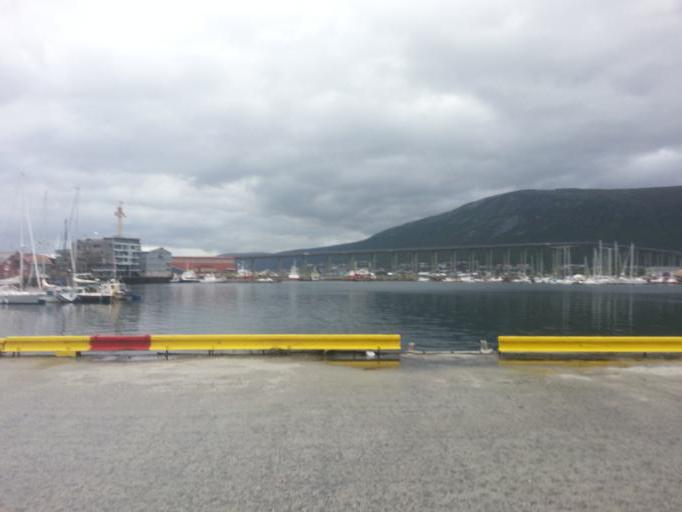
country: NO
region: Troms
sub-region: Tromso
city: Tromso
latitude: 69.6502
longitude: 18.9603
